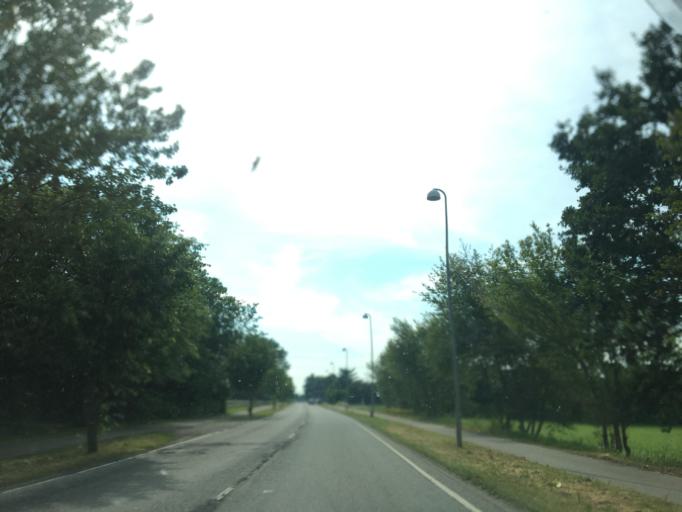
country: DK
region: Zealand
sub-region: Greve Kommune
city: Tune
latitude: 55.5976
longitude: 12.2141
